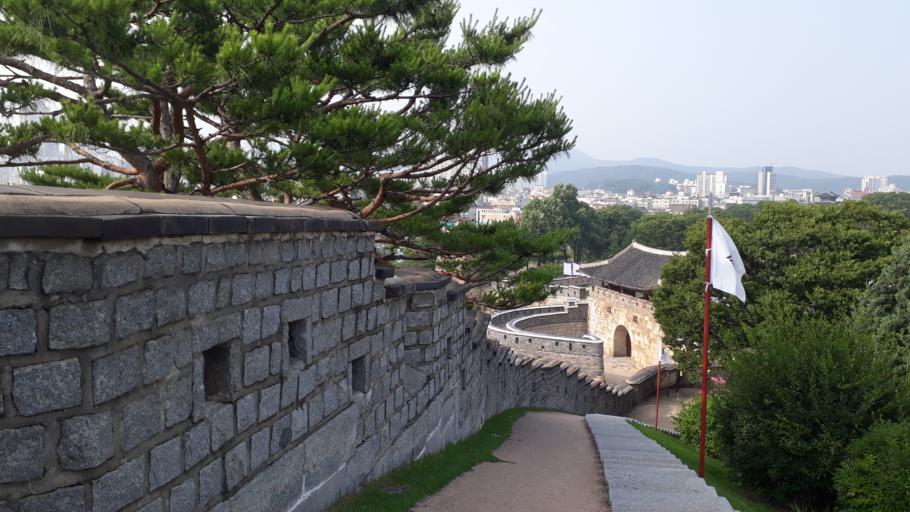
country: KR
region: Gyeonggi-do
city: Suwon-si
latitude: 37.2875
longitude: 127.0181
